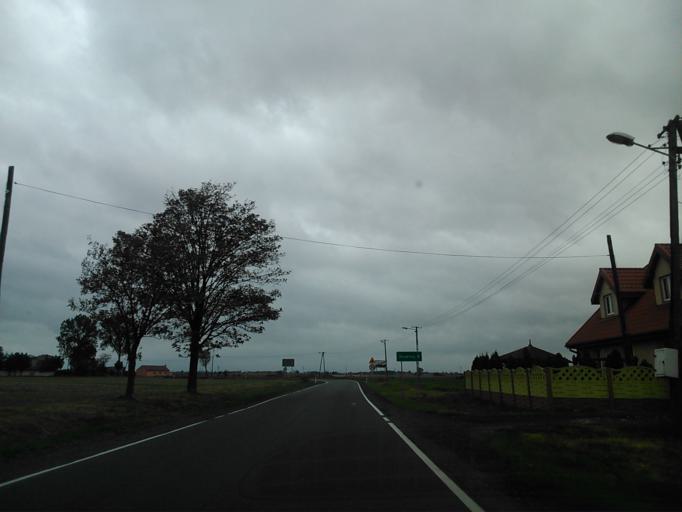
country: PL
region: Kujawsko-Pomorskie
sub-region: Powiat inowroclawski
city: Kruszwica
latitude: 52.6818
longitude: 18.2627
